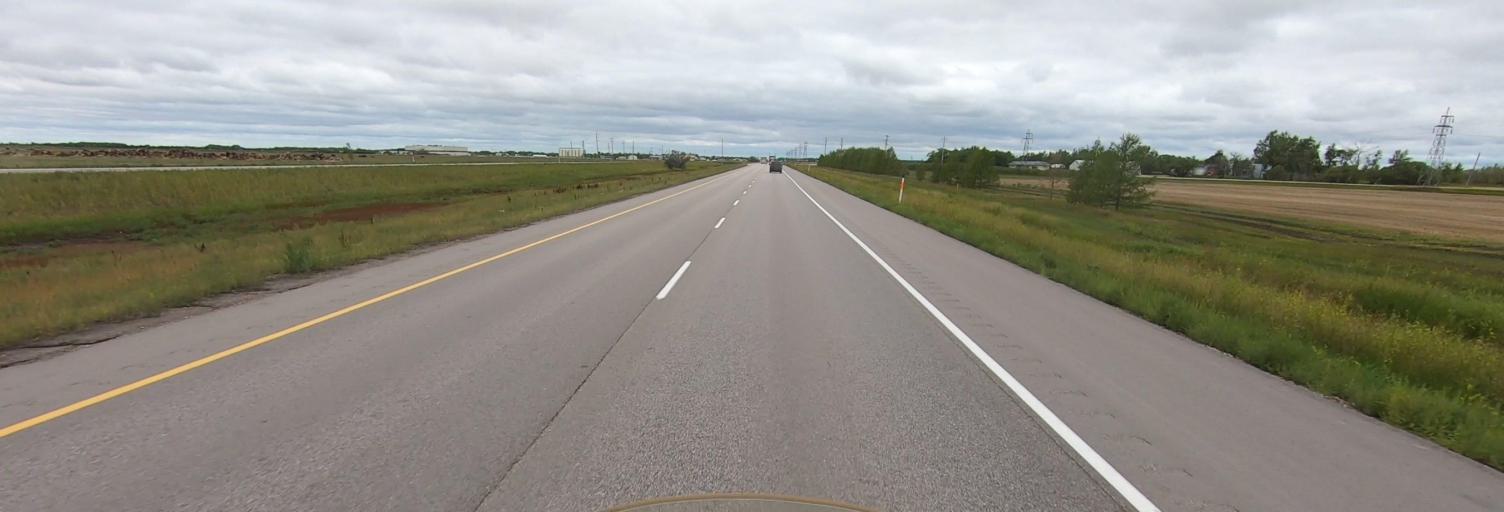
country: CA
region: Manitoba
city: Headingley
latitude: 49.8996
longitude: -97.7174
